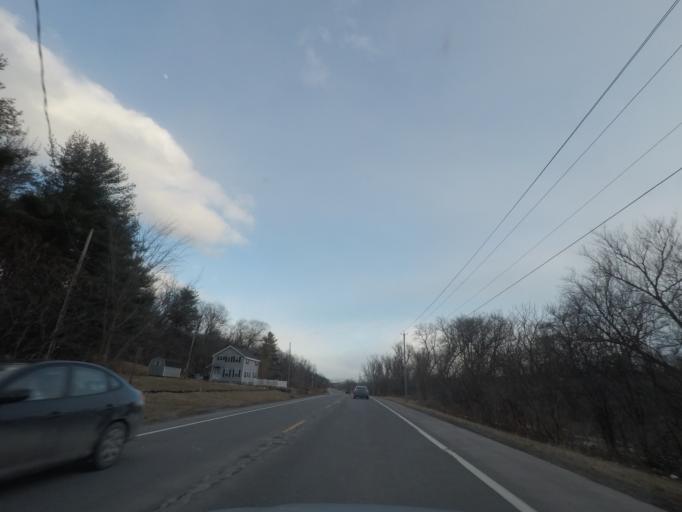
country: US
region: New York
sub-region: Herkimer County
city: Frankfort
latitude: 43.0373
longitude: -75.0545
